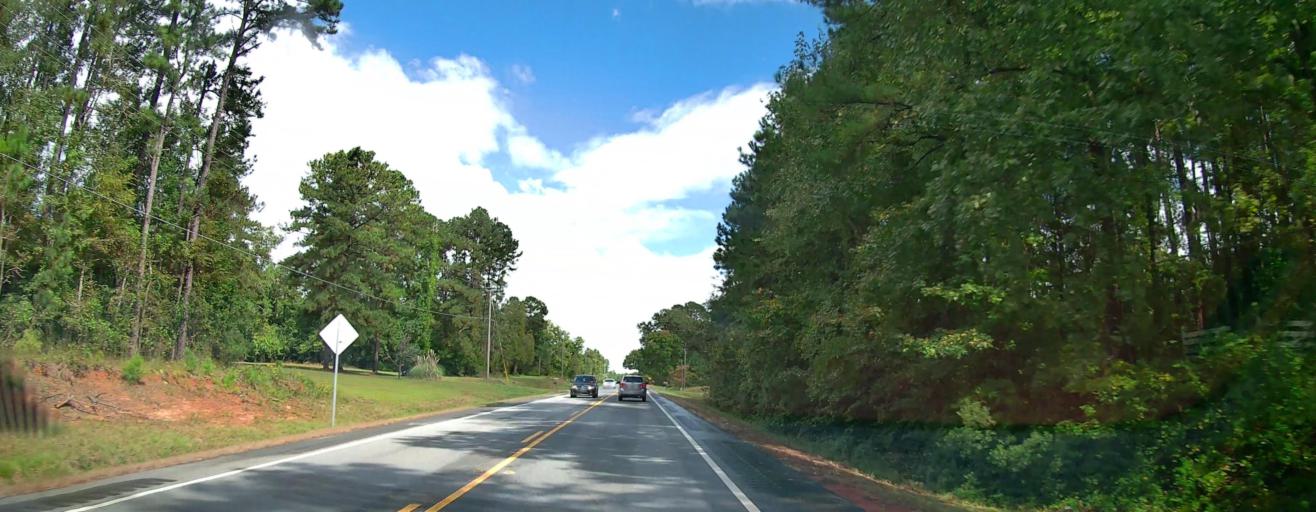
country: US
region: Georgia
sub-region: Baldwin County
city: Milledgeville
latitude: 33.0367
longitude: -83.3079
